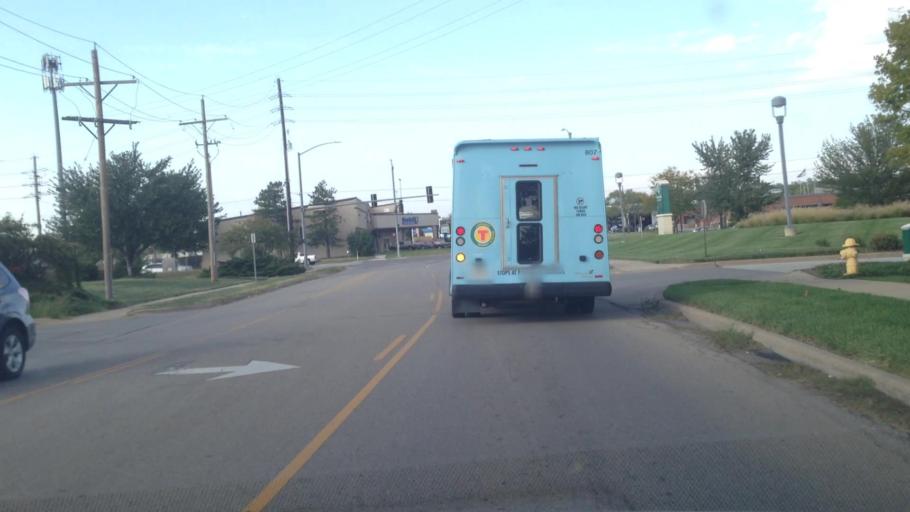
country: US
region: Kansas
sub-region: Douglas County
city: Lawrence
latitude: 38.9271
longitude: -95.2625
